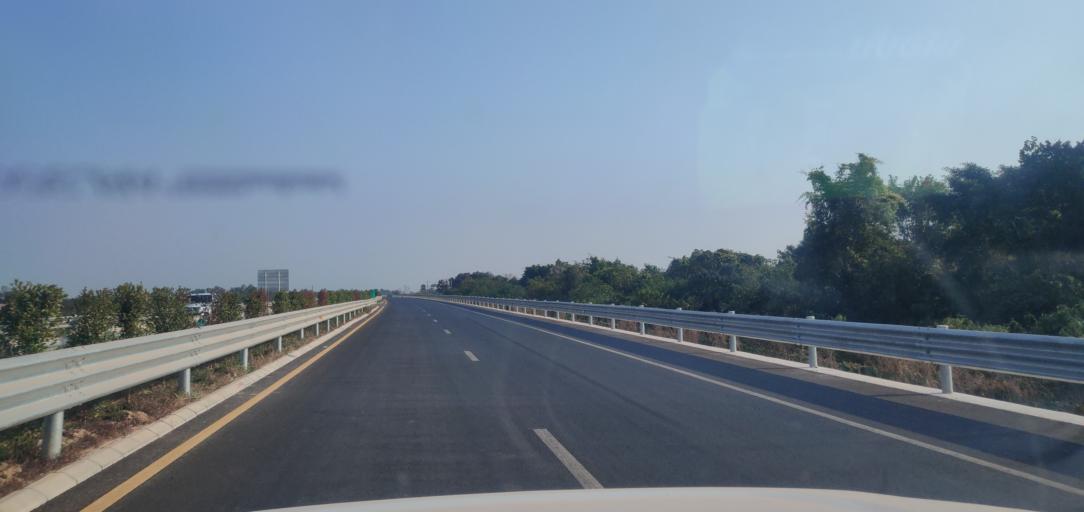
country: LA
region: Vientiane
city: Muang Phon-Hong
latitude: 18.2926
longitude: 102.4582
